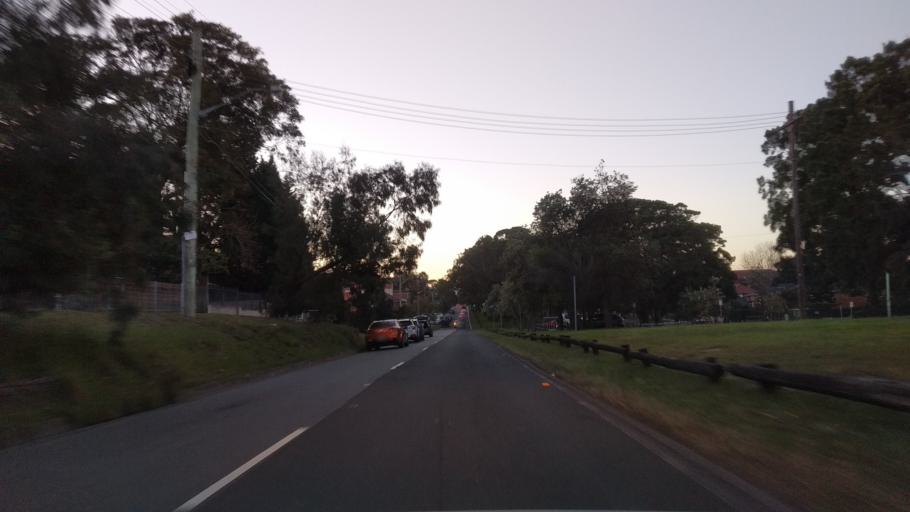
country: AU
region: New South Wales
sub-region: Randwick
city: Maroubra
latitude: -33.9496
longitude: 151.2410
